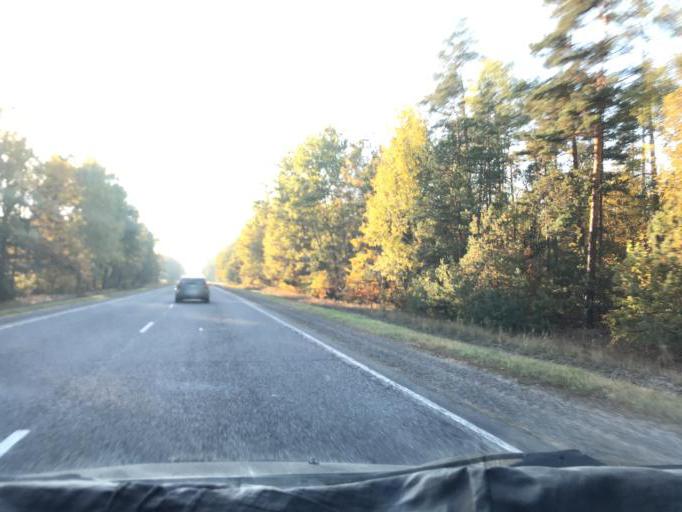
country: BY
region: Gomel
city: Zhytkavichy
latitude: 52.2722
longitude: 27.9990
